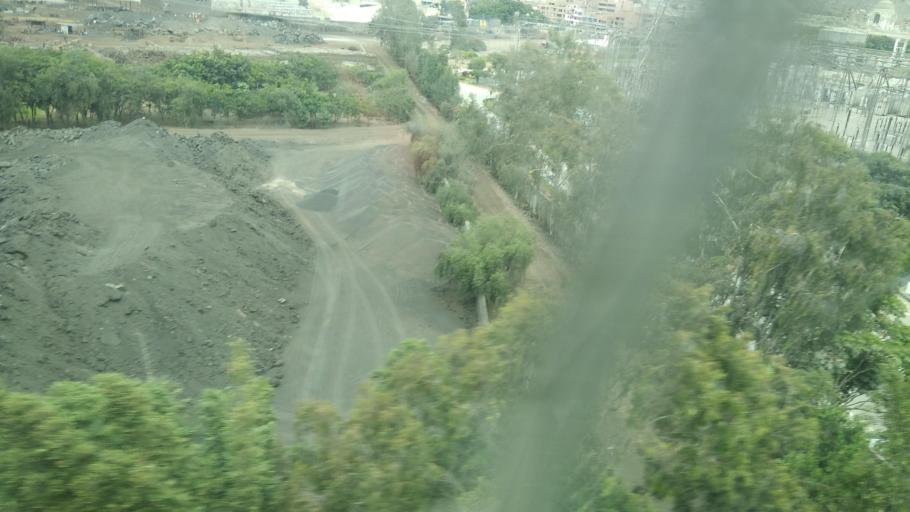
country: PE
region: Lima
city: Lima
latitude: -12.0377
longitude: -77.0127
